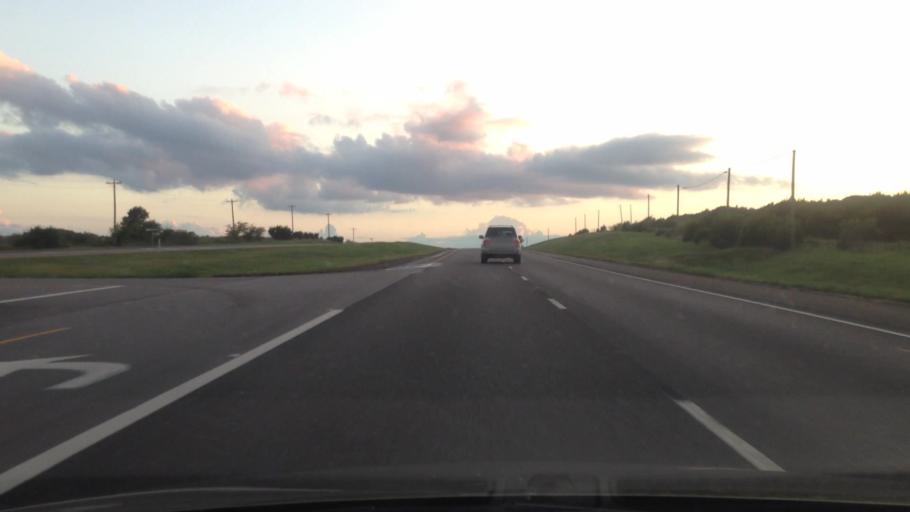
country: US
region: Texas
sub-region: Parker County
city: Aledo
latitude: 32.5958
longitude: -97.5796
